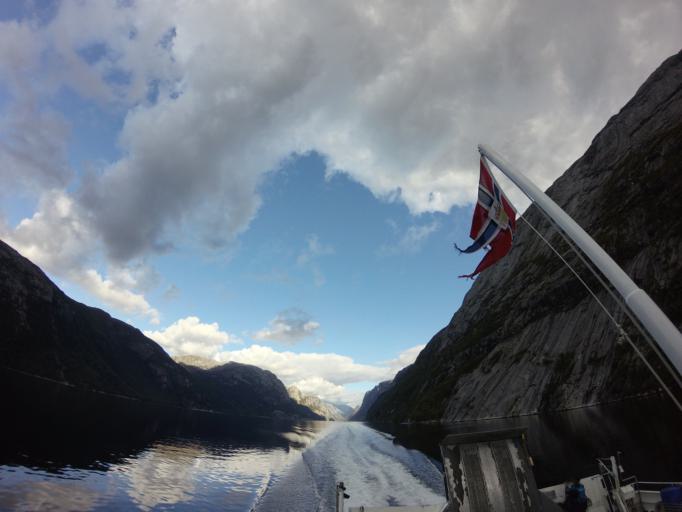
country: NO
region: Rogaland
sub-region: Hjelmeland
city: Hjelmelandsvagen
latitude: 59.0219
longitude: 6.4558
